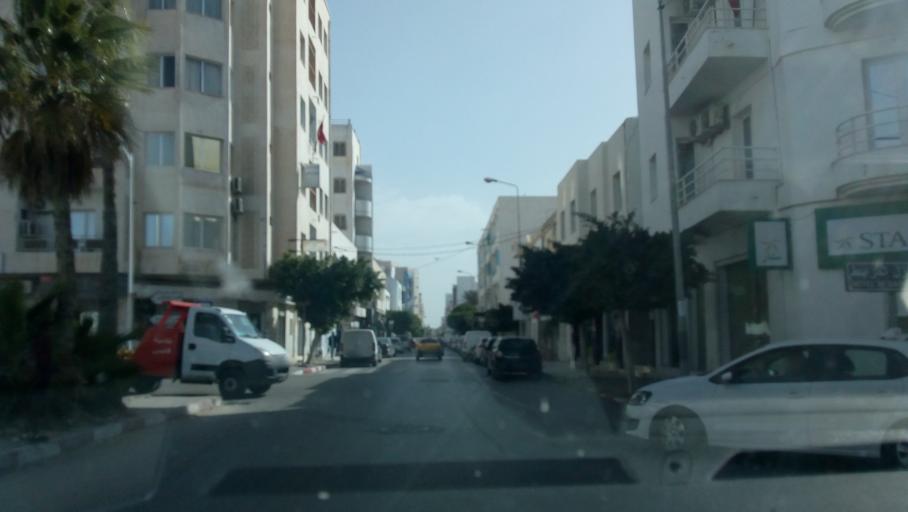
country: TN
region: Qabis
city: Gabes
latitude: 33.8858
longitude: 10.1000
